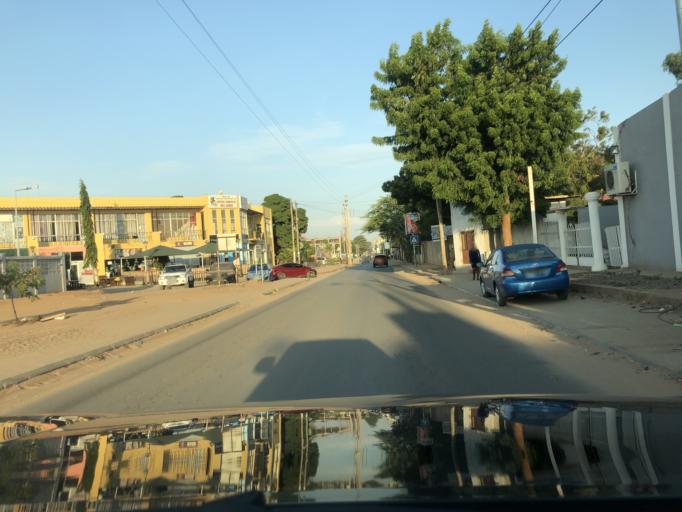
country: AO
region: Luanda
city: Luanda
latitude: -8.9487
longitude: 13.1682
